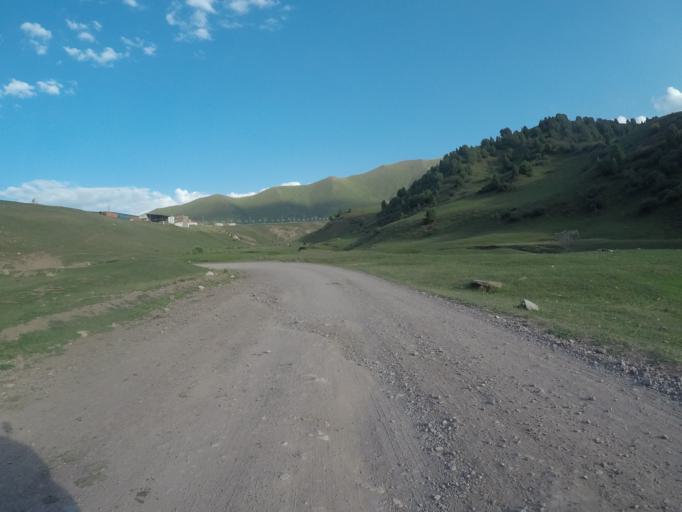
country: KG
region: Chuy
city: Bishkek
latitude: 42.6406
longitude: 74.6248
